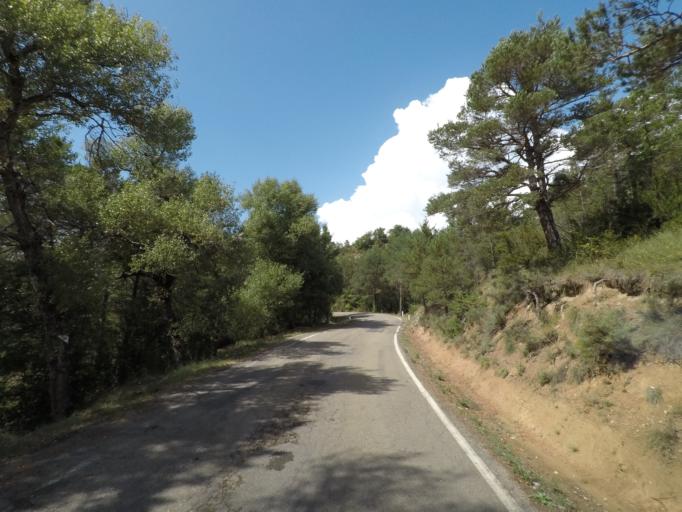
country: ES
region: Aragon
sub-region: Provincia de Huesca
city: Yebra de Basa
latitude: 42.3931
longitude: -0.3209
